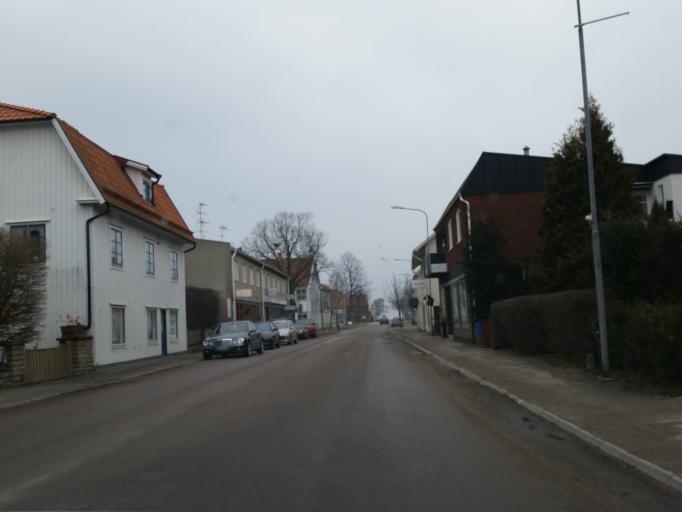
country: SE
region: Kalmar
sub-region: Morbylanga Kommun
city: Moerbylanga
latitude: 56.5265
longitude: 16.3777
